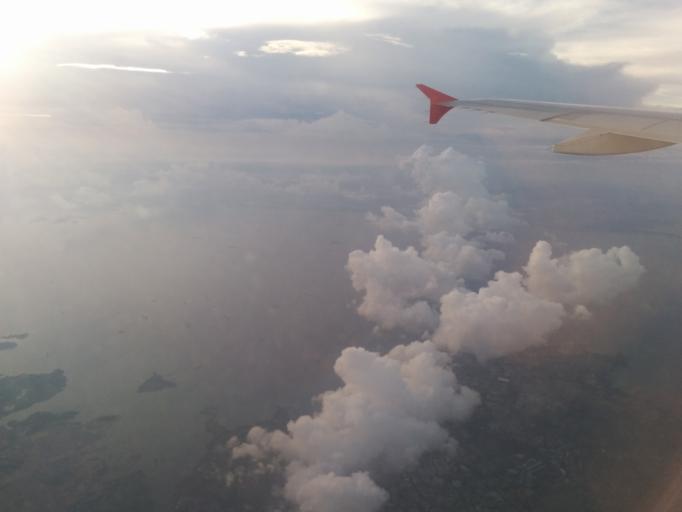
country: SG
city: Singapore
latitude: 1.0941
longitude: 104.0290
